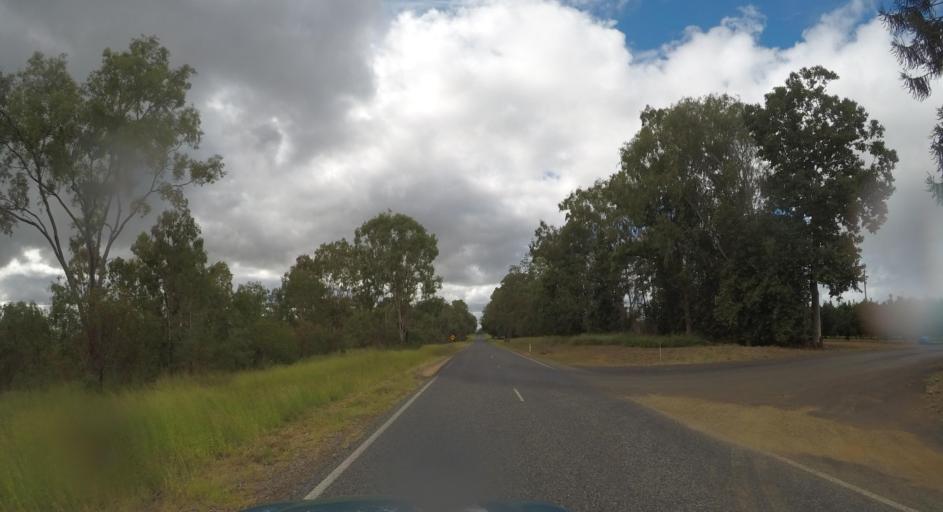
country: AU
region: Queensland
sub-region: North Burnett
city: Gayndah
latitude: -25.6293
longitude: 151.2830
